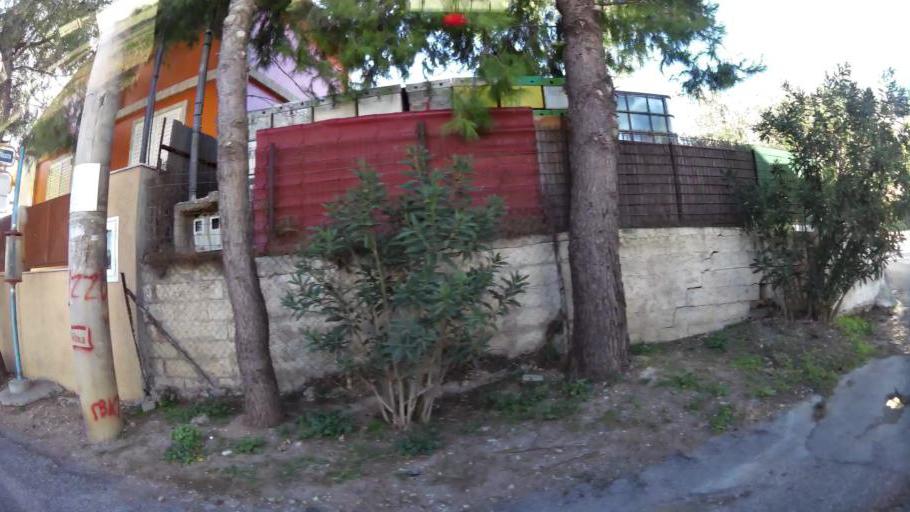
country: GR
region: Attica
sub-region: Nomarchia Anatolikis Attikis
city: Acharnes
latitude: 38.0961
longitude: 23.7192
